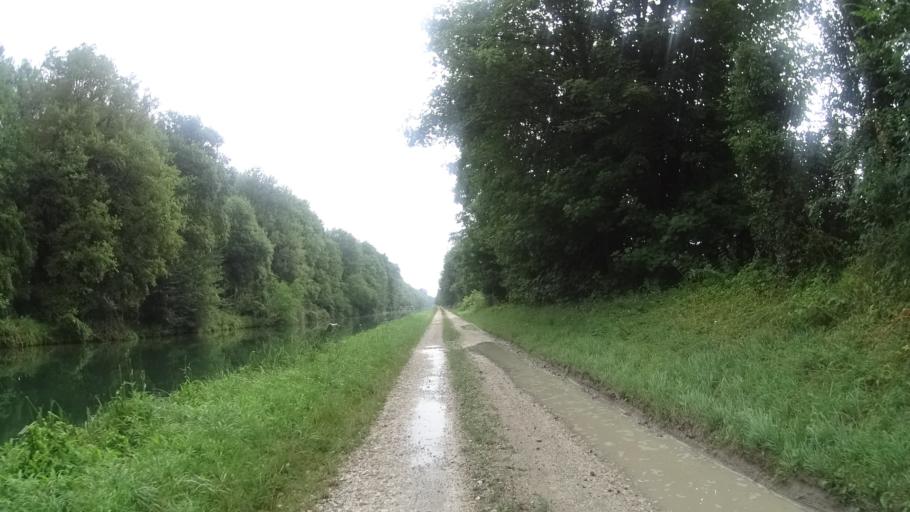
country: FR
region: Bourgogne
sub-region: Departement de l'Yonne
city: Brienon-sur-Armancon
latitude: 47.9851
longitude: 3.5845
